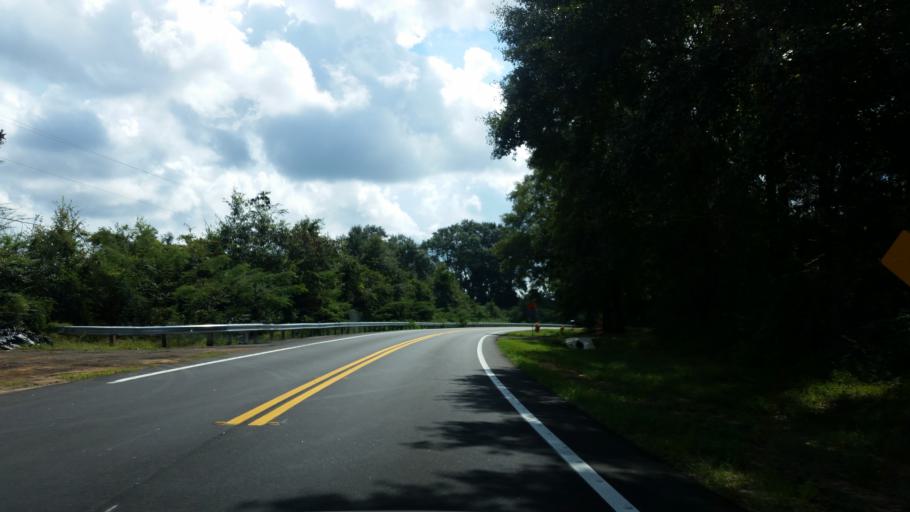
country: US
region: Florida
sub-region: Escambia County
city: Molino
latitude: 30.6916
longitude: -87.4056
